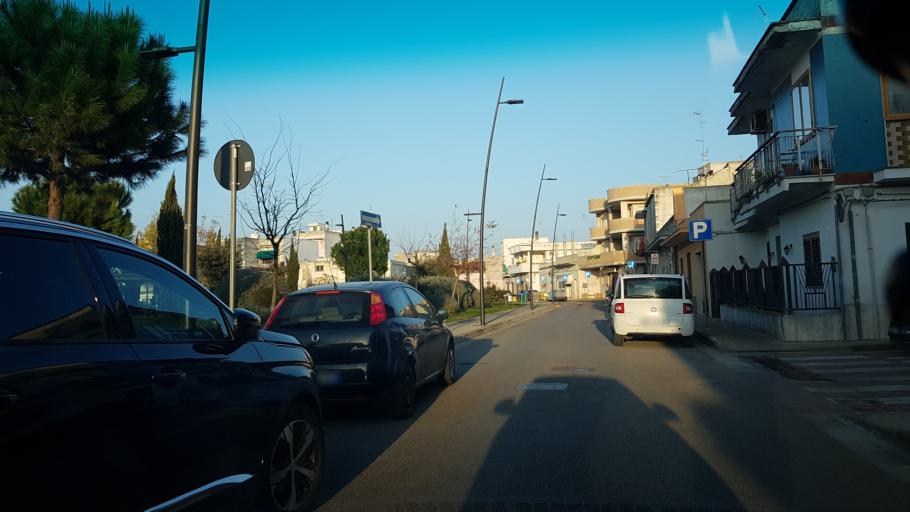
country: IT
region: Apulia
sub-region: Provincia di Brindisi
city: Mesagne
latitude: 40.5576
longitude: 17.7987
